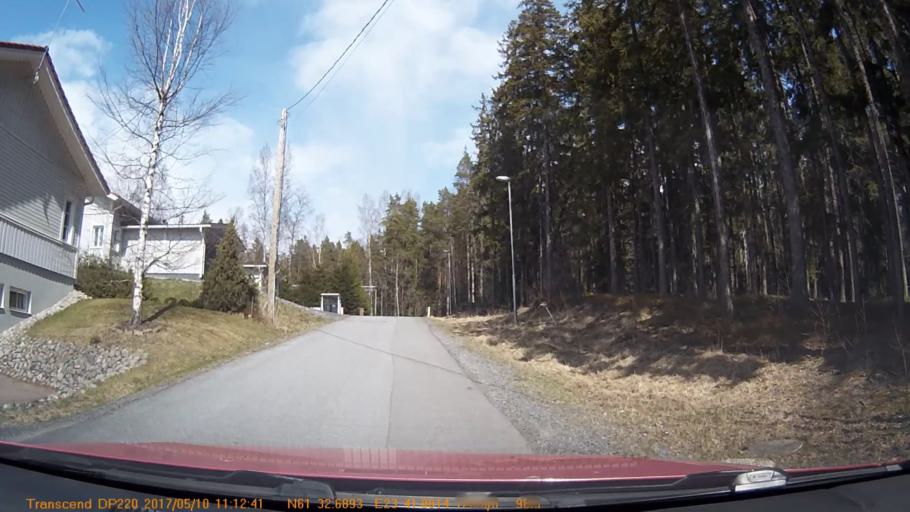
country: FI
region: Pirkanmaa
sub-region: Tampere
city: Yloejaervi
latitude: 61.5448
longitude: 23.6847
